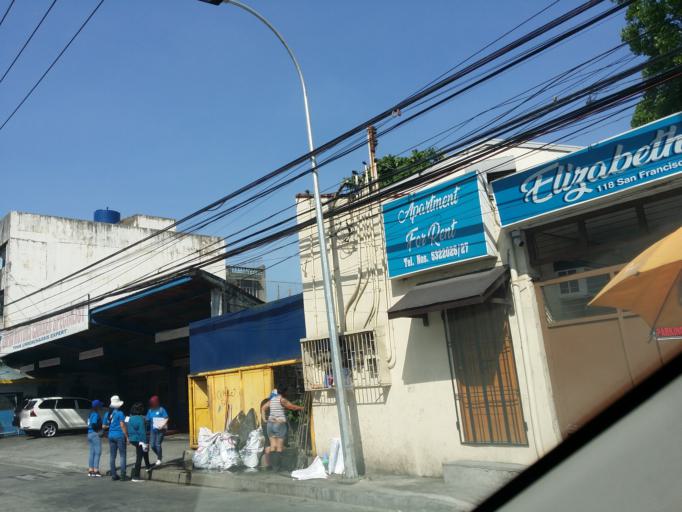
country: PH
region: Metro Manila
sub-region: Mandaluyong
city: Mandaluyong City
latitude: 14.5762
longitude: 121.0325
